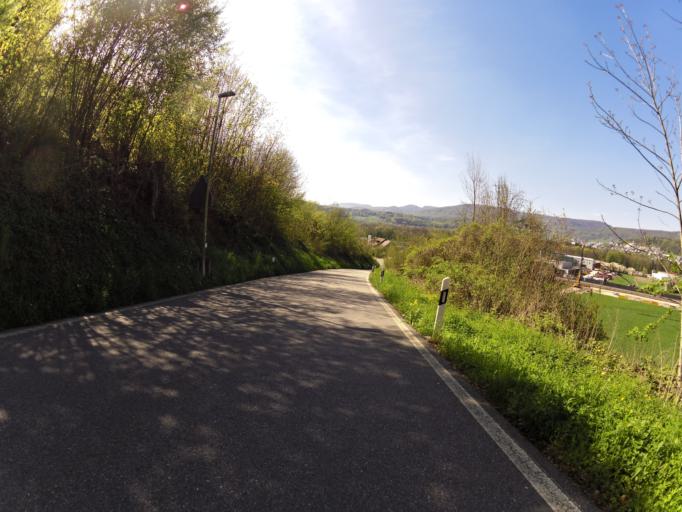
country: CH
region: Aargau
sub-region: Bezirk Aarau
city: Aarau
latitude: 47.3831
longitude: 8.0289
